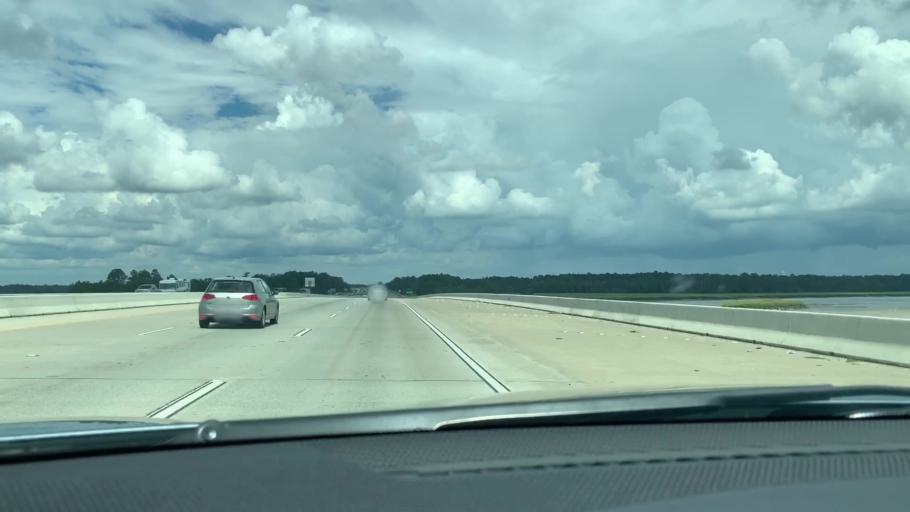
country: US
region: Georgia
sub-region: Glynn County
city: Dock Junction
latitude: 31.1516
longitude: -81.5648
